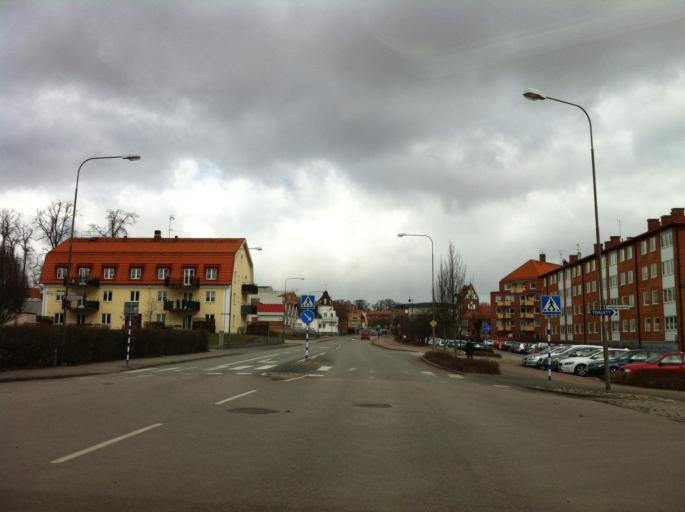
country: SE
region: Skane
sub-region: Kristianstads Kommun
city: Fjalkinge
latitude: 56.0402
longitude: 14.3512
